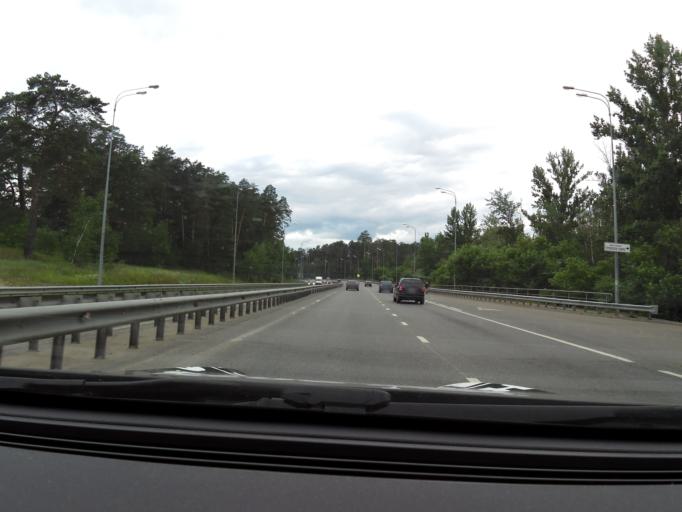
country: RU
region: Tatarstan
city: Staroye Arakchino
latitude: 55.8333
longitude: 48.9829
